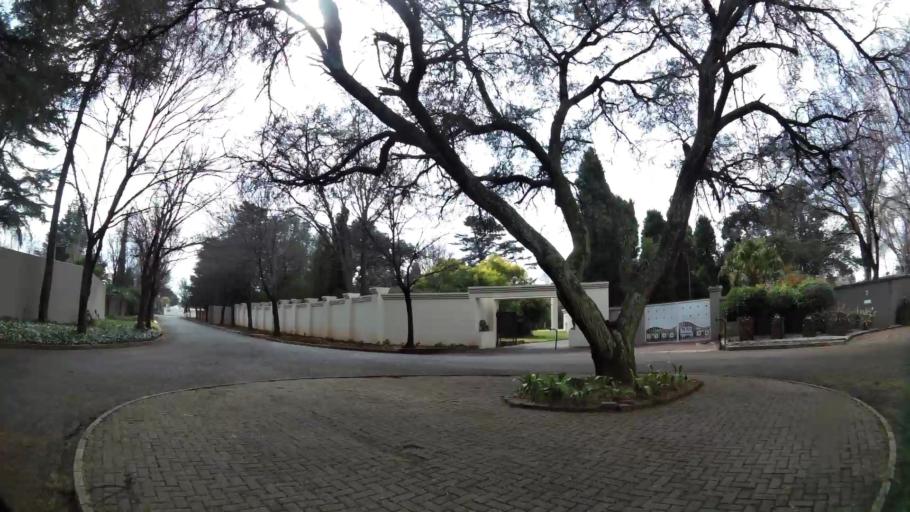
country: ZA
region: Gauteng
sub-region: Sedibeng District Municipality
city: Vanderbijlpark
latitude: -26.7432
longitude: 27.8339
